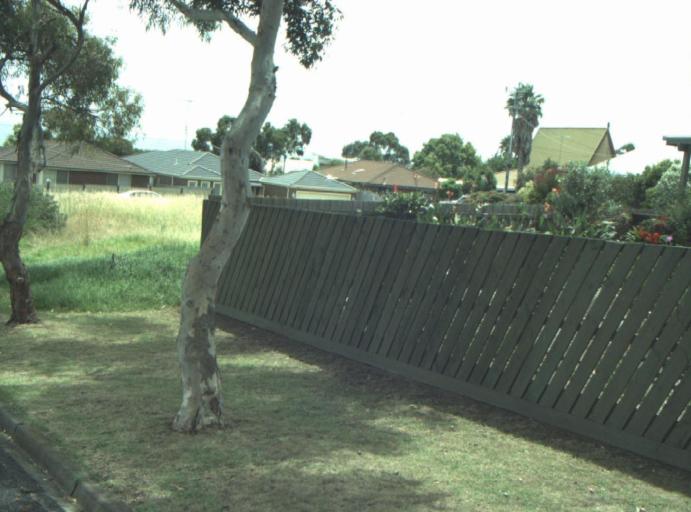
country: AU
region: Victoria
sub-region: Greater Geelong
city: Clifton Springs
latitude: -38.1591
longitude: 144.5524
